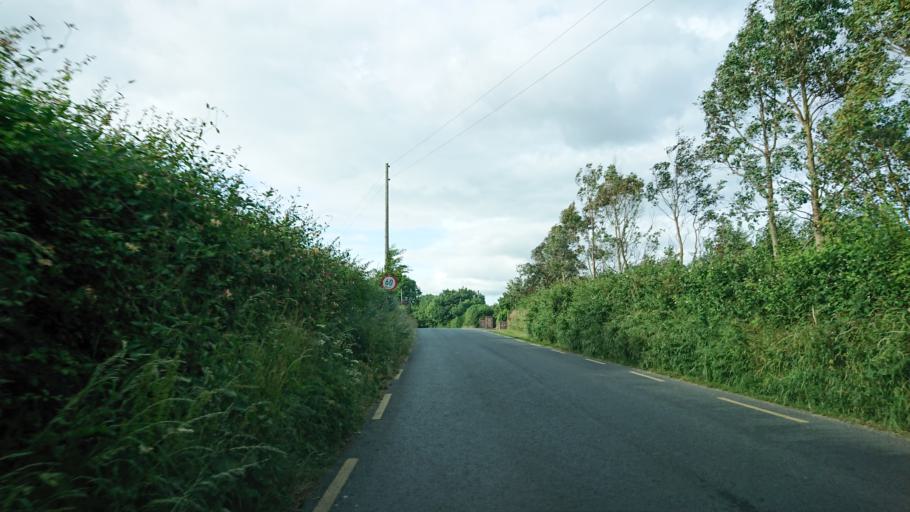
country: IE
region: Munster
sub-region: Waterford
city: Waterford
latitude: 52.2335
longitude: -7.1586
